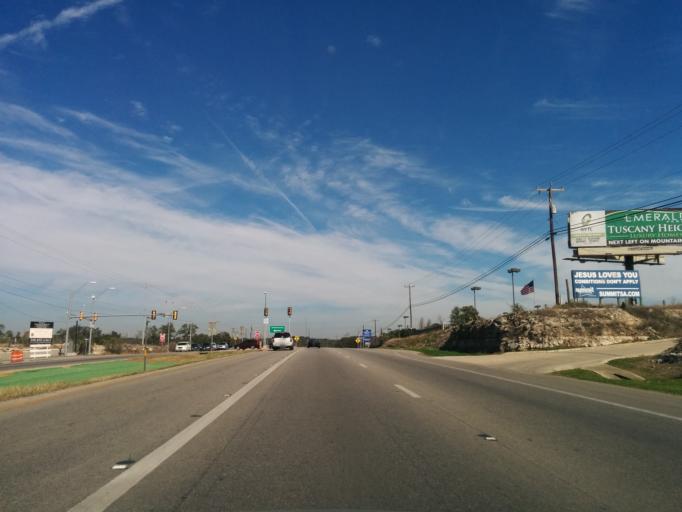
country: US
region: Texas
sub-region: Bexar County
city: Timberwood Park
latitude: 29.6625
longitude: -98.4500
